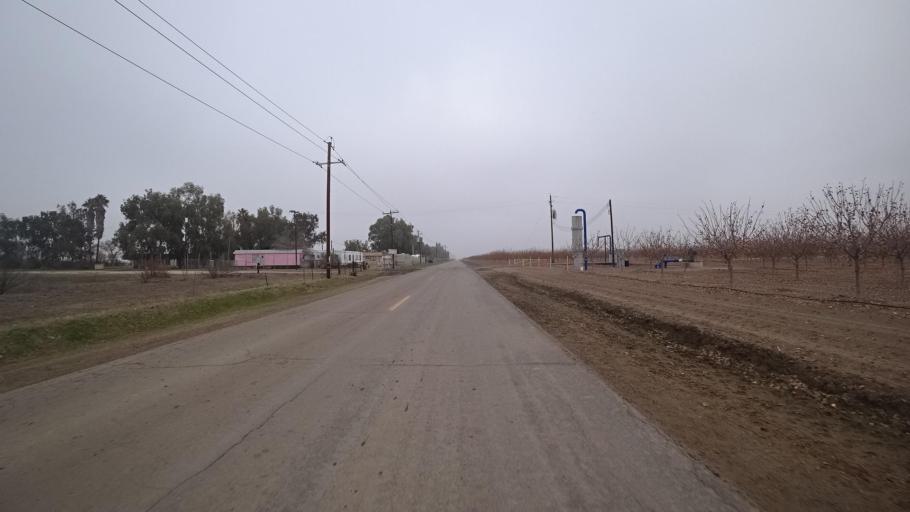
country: US
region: California
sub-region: Kern County
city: Wasco
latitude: 35.6877
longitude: -119.5087
